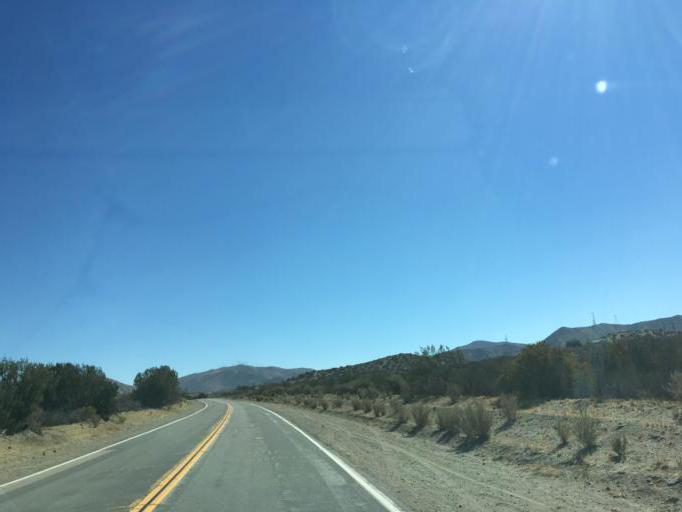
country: US
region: California
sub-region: Los Angeles County
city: Acton
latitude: 34.4750
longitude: -118.1545
